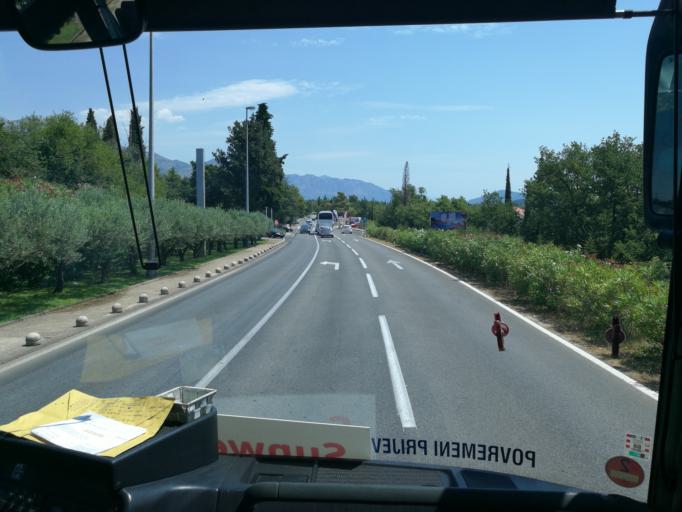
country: HR
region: Dubrovacko-Neretvanska
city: Jasenice
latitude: 42.5591
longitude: 18.2604
